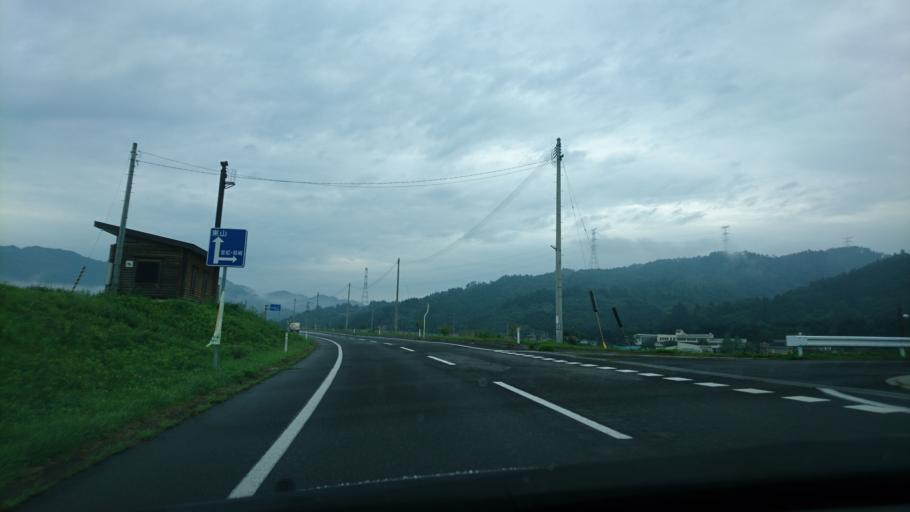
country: JP
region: Iwate
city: Ichinoseki
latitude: 38.9283
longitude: 141.2576
